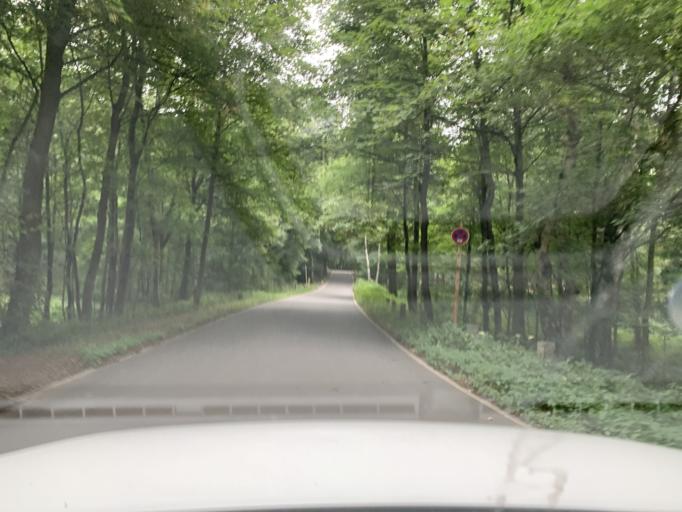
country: DE
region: North Rhine-Westphalia
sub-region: Regierungsbezirk Dusseldorf
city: Hochfeld
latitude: 51.3786
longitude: 6.8160
